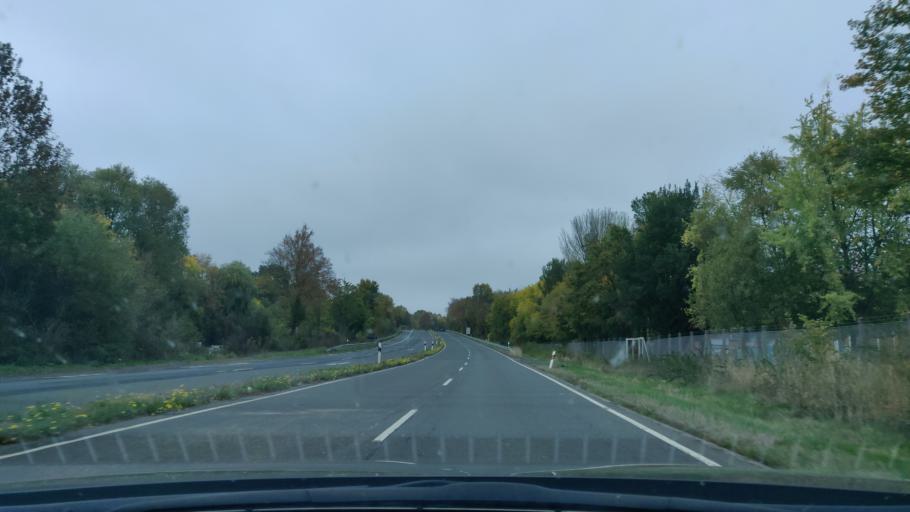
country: DE
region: Hesse
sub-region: Regierungsbezirk Kassel
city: Baunatal
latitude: 51.2539
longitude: 9.4224
